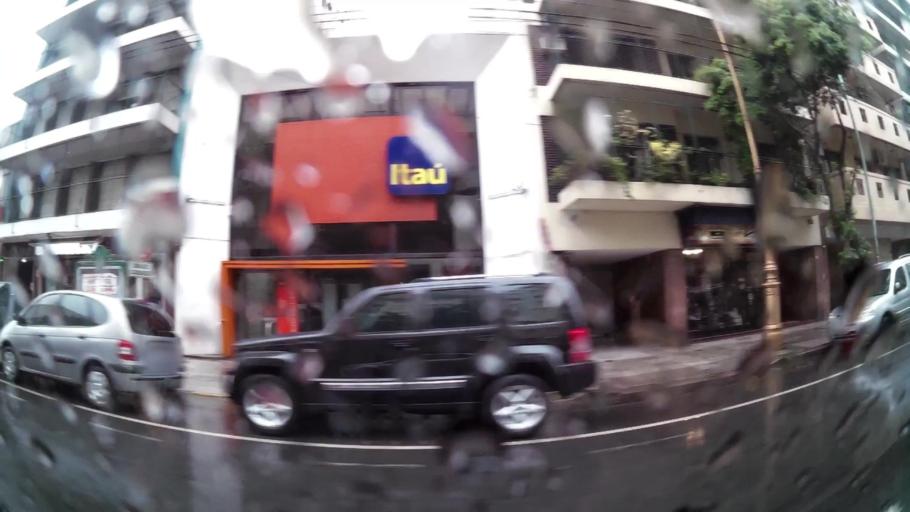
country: AR
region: Buenos Aires
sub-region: Partido de Avellaneda
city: Avellaneda
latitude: -34.6400
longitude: -58.3743
